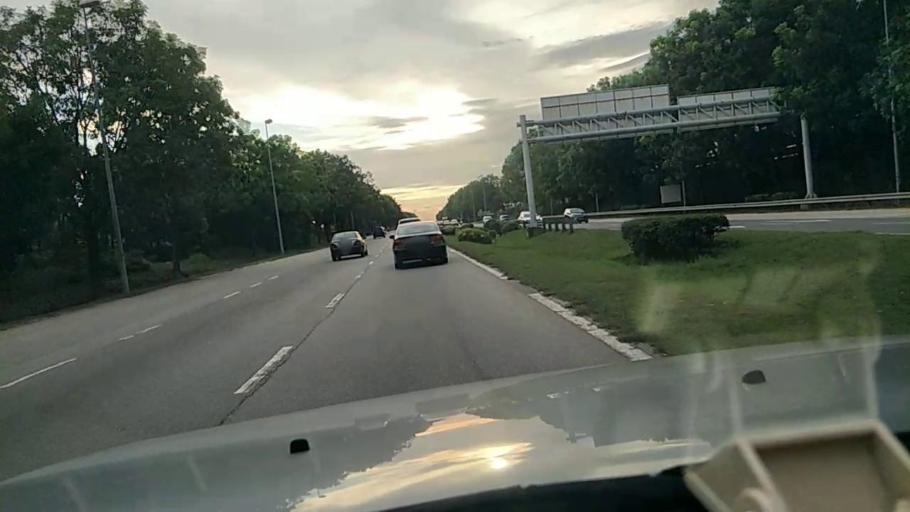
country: MY
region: Selangor
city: Klang
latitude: 3.1080
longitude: 101.4525
